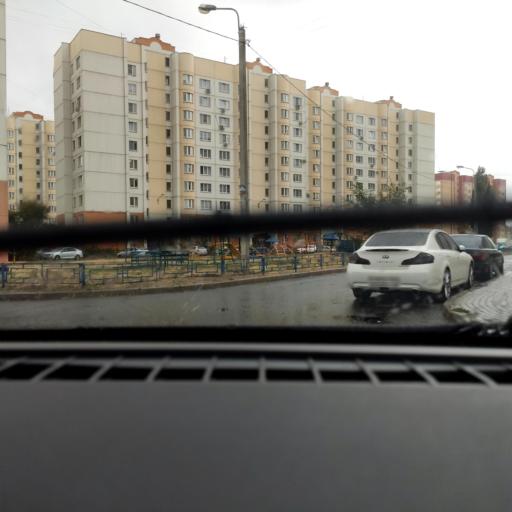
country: RU
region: Voronezj
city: Maslovka
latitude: 51.6023
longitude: 39.2428
